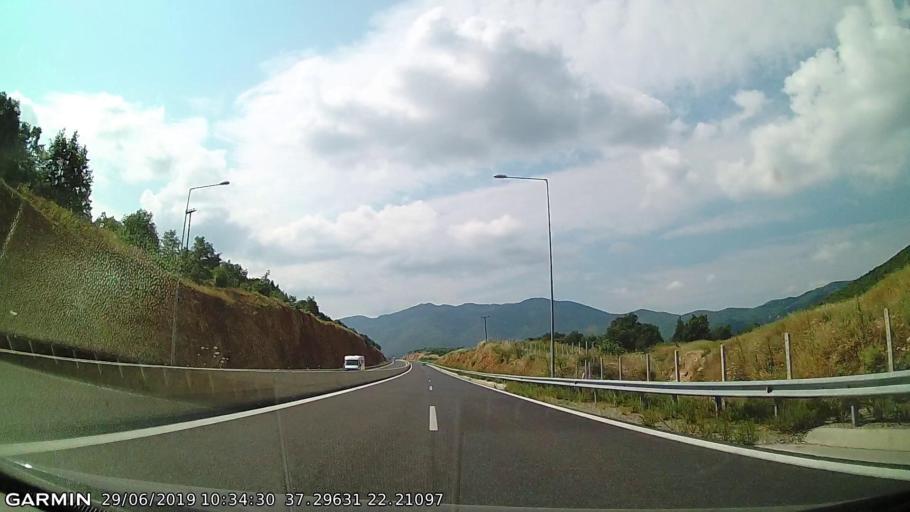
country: GR
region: Peloponnese
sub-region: Nomos Arkadias
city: Megalopoli
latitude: 37.2961
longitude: 22.2110
